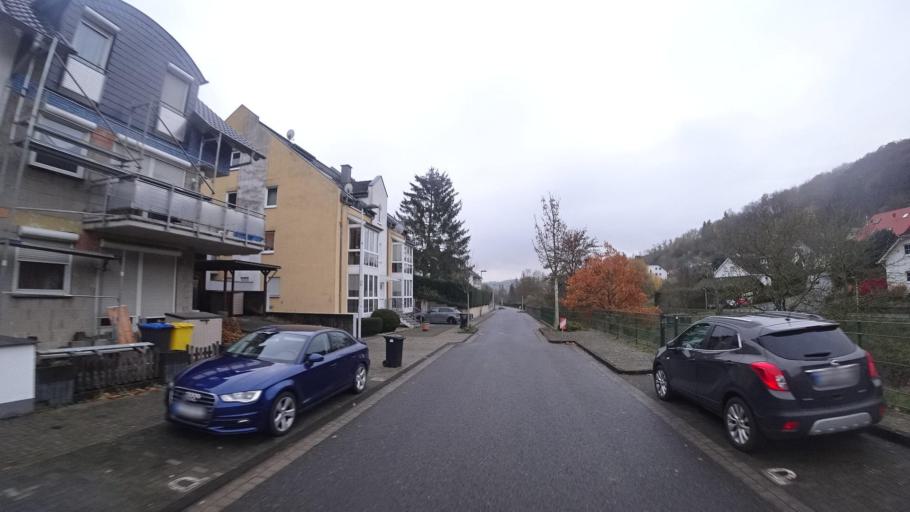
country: DE
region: Rheinland-Pfalz
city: Remagen
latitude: 50.5539
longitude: 7.1855
